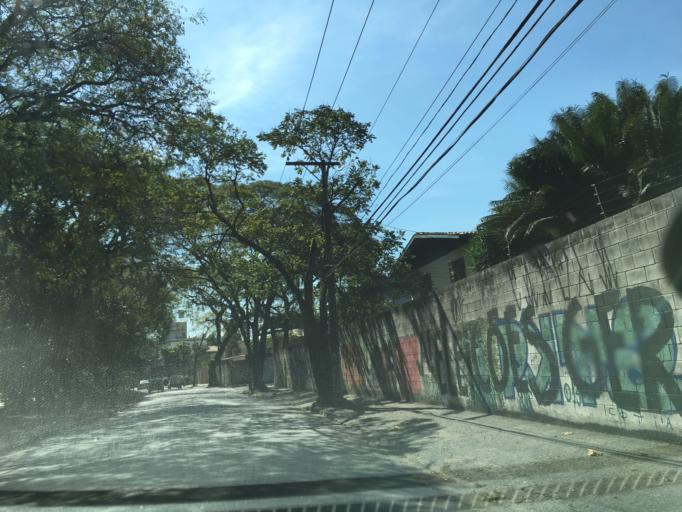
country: BR
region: Sao Paulo
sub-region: Sao Paulo
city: Sao Paulo
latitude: -23.5648
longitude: -46.7067
